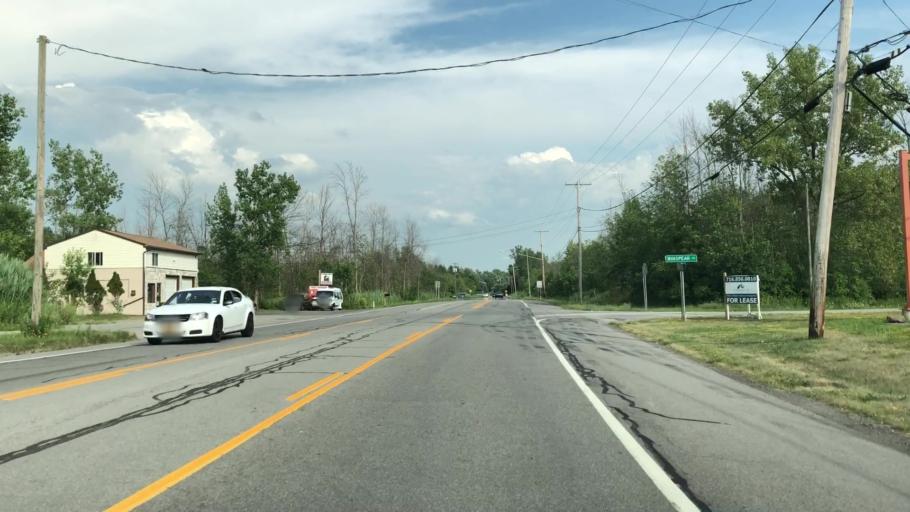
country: US
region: New York
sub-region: Erie County
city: Lancaster
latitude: 42.8585
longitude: -78.6753
